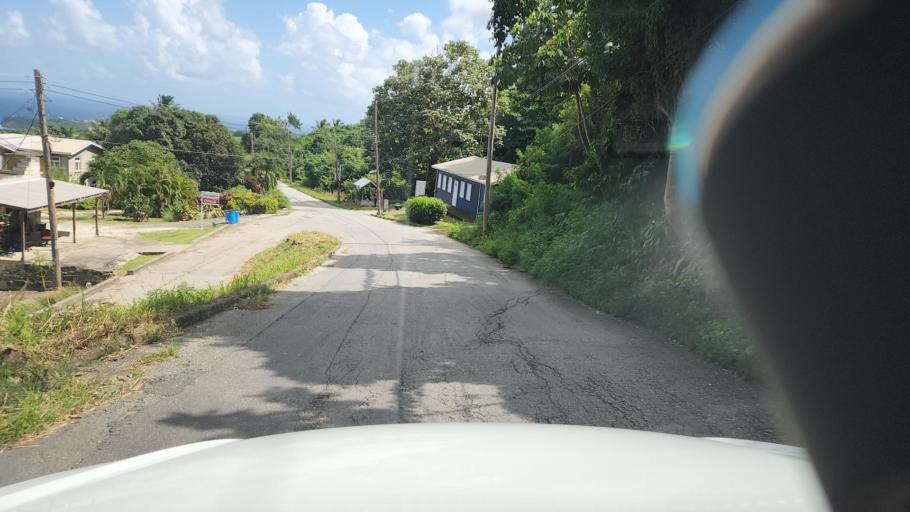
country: BB
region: Saint John
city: Four Cross Roads
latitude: 13.1807
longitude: -59.4834
